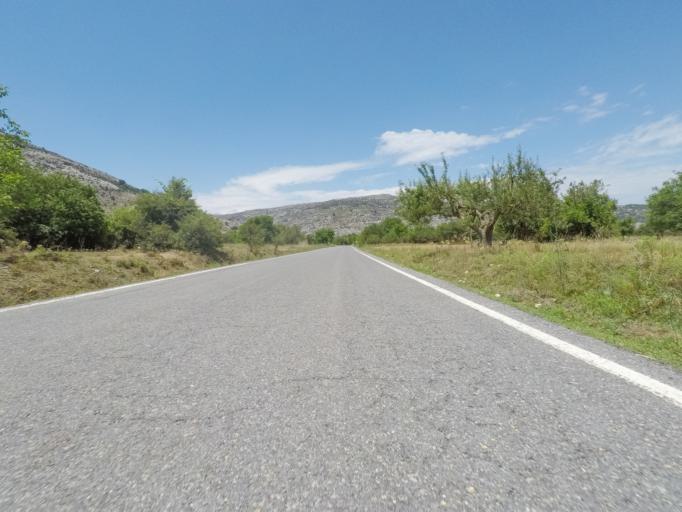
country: GR
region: Crete
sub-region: Nomos Irakleiou
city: Mokhos
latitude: 35.1817
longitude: 25.4333
